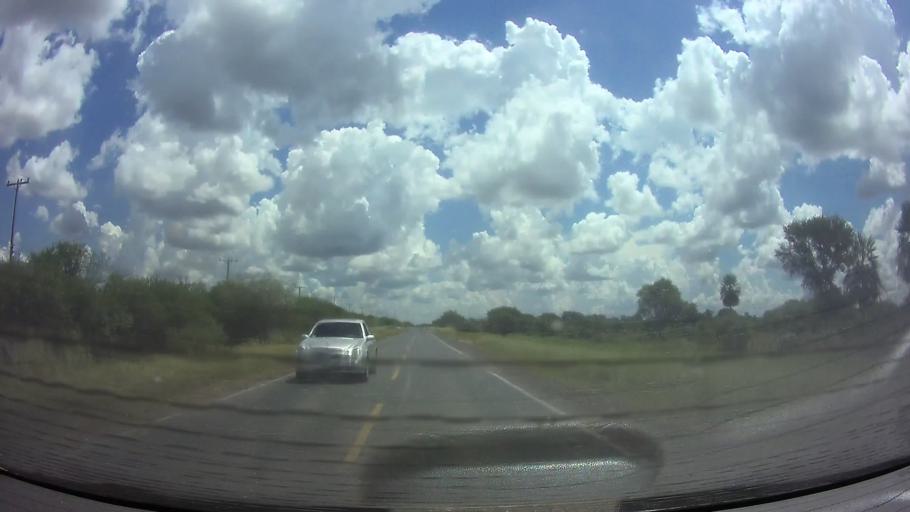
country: PY
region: Central
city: Colonia Mariano Roque Alonso
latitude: -25.1884
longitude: -57.6046
